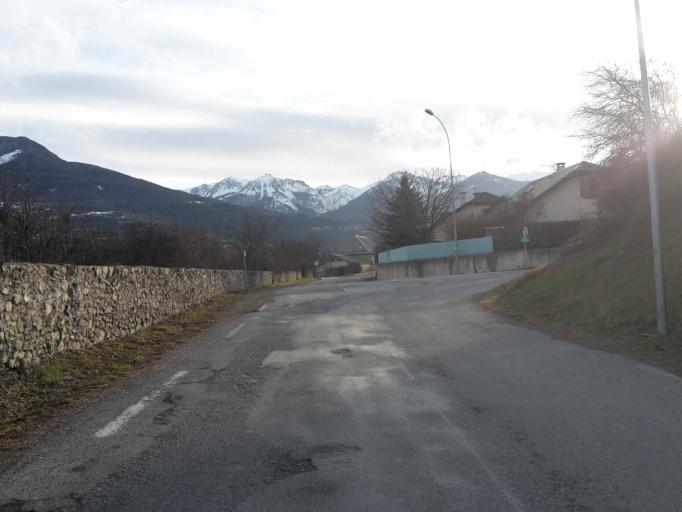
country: FR
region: Provence-Alpes-Cote d'Azur
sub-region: Departement des Hautes-Alpes
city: Embrun
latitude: 44.5559
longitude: 6.4871
